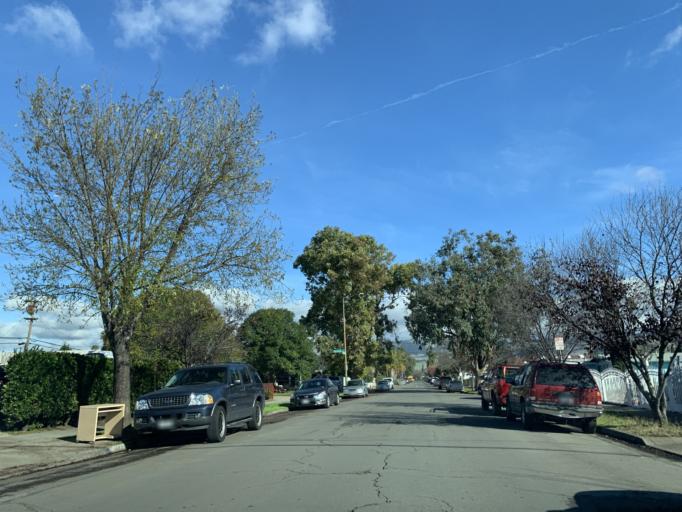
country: US
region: California
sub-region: Santa Clara County
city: Alum Rock
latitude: 37.3347
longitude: -121.8364
